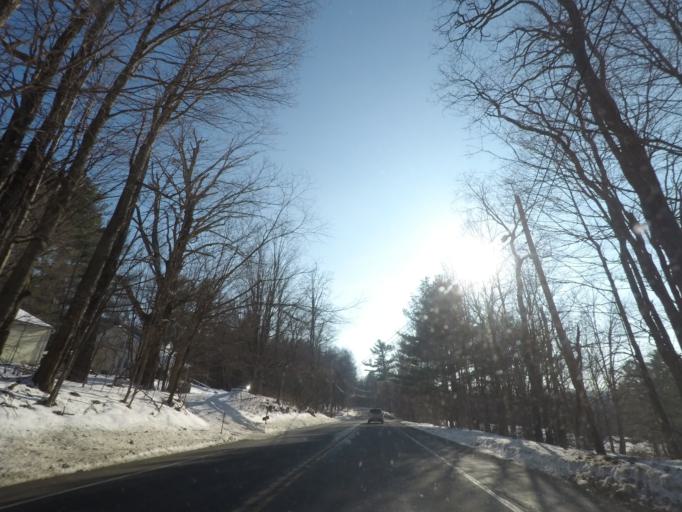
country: US
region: Massachusetts
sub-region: Berkshire County
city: Richmond
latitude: 42.4973
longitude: -73.3703
